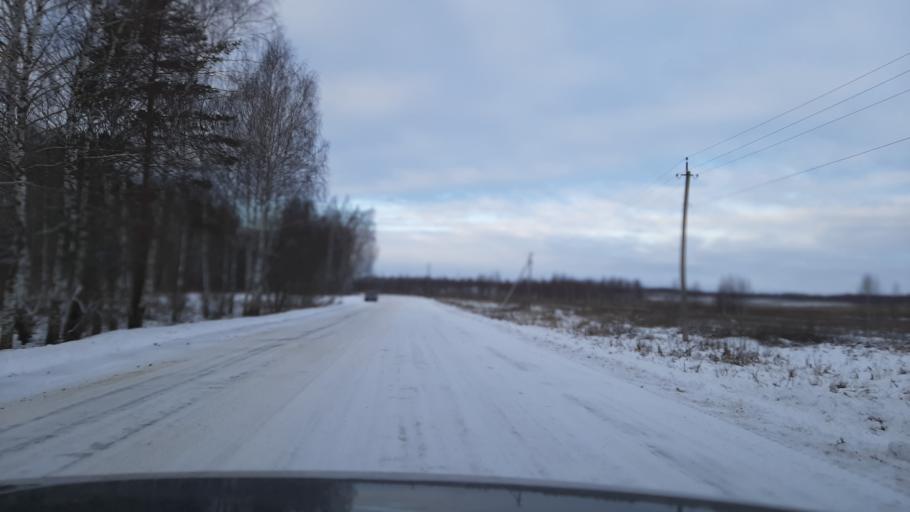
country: RU
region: Kostroma
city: Nerekhta
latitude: 57.4714
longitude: 40.6721
